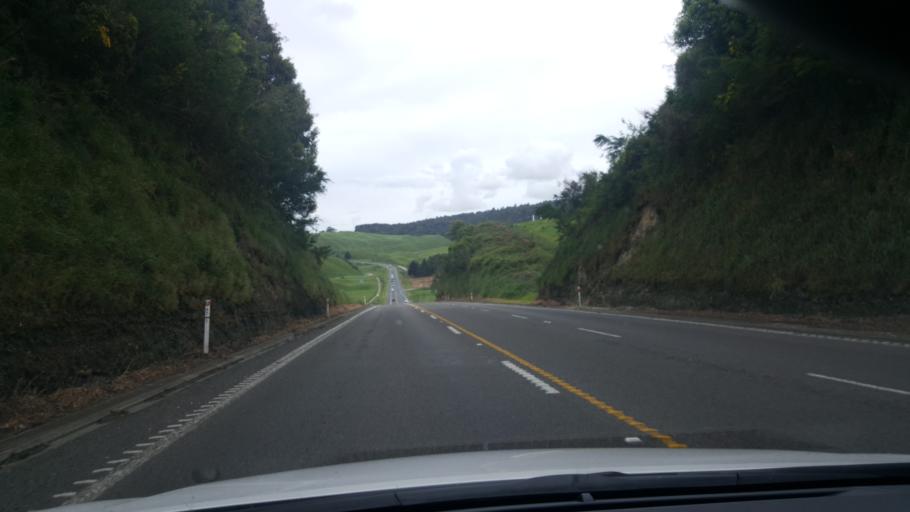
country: NZ
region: Bay of Plenty
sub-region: Rotorua District
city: Rotorua
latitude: -38.2511
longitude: 176.3181
